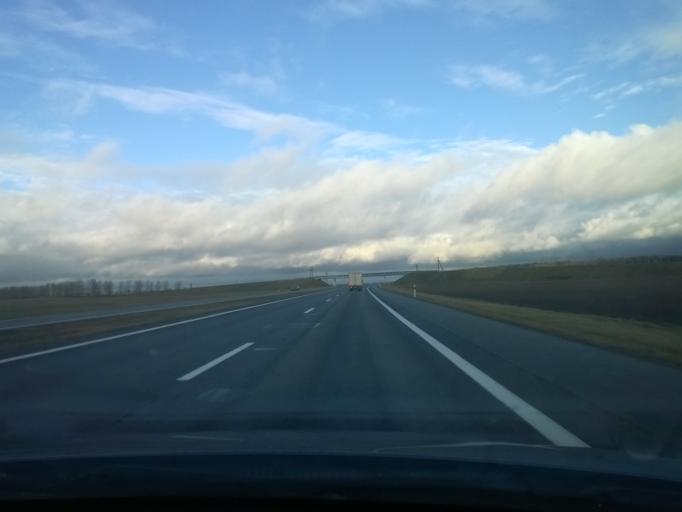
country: BY
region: Brest
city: Haradzishcha
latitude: 53.2332
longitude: 26.1730
